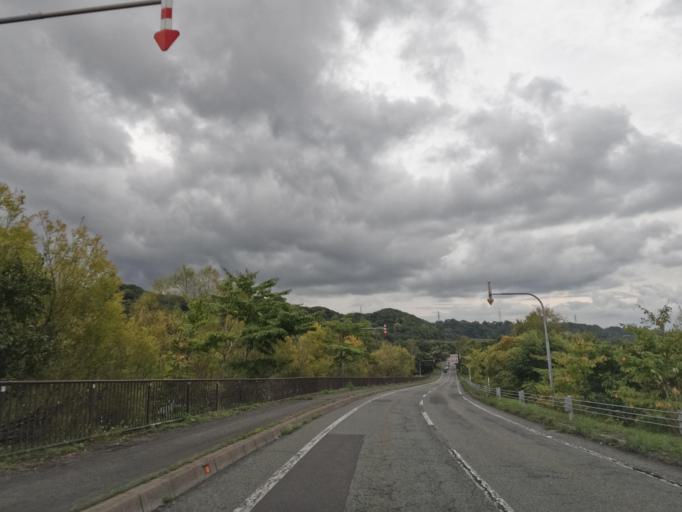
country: JP
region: Hokkaido
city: Date
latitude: 42.5191
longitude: 140.8634
